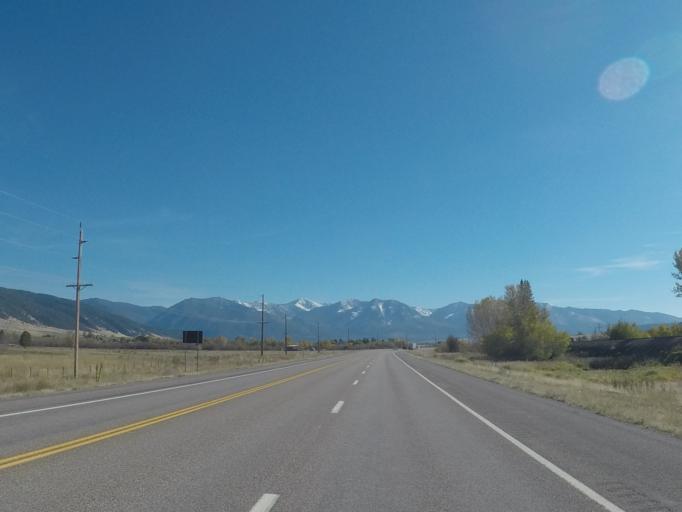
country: US
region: Montana
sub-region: Missoula County
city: Frenchtown
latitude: 47.2007
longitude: -114.1090
